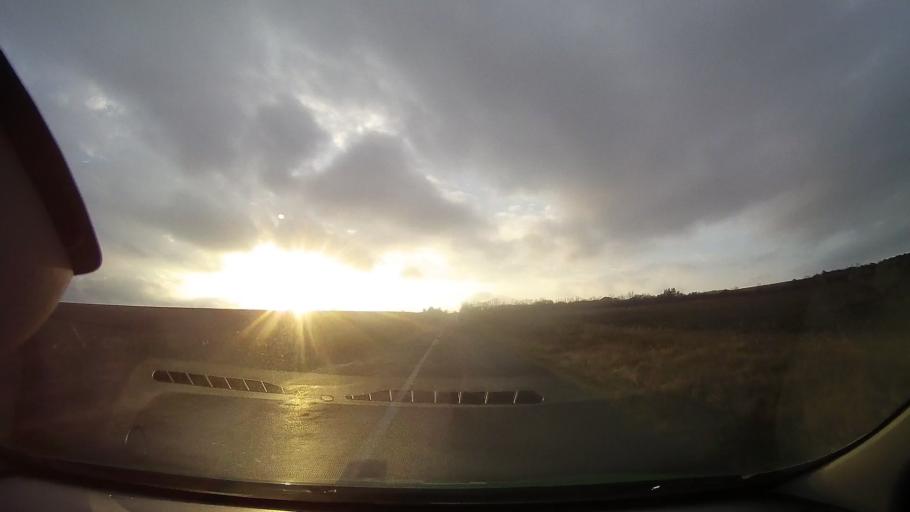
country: RO
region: Constanta
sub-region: Comuna Adamclisi
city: Adamclisi
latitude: 44.0347
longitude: 27.9364
